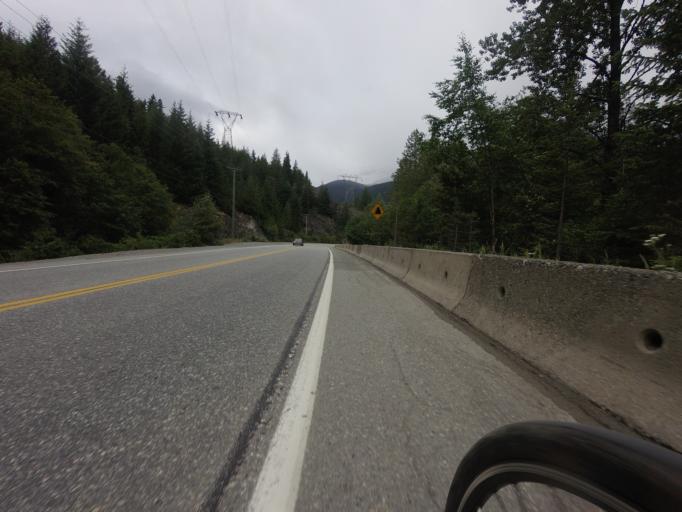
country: CA
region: British Columbia
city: Whistler
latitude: 50.1702
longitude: -122.8897
